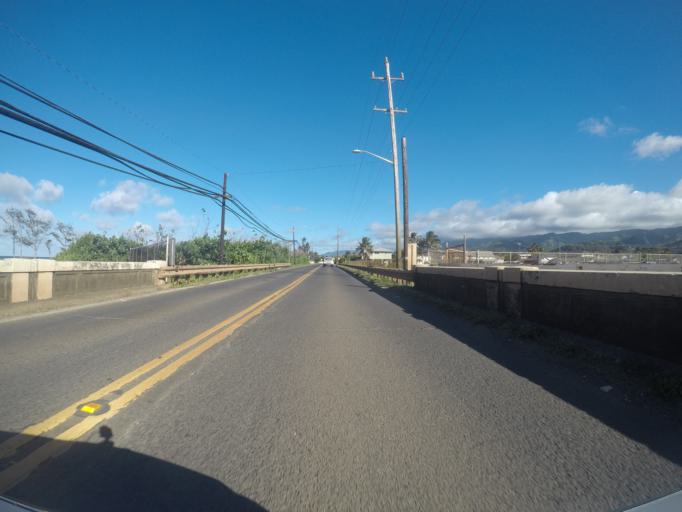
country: US
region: Hawaii
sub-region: Honolulu County
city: La'ie
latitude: 21.6540
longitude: -157.9299
